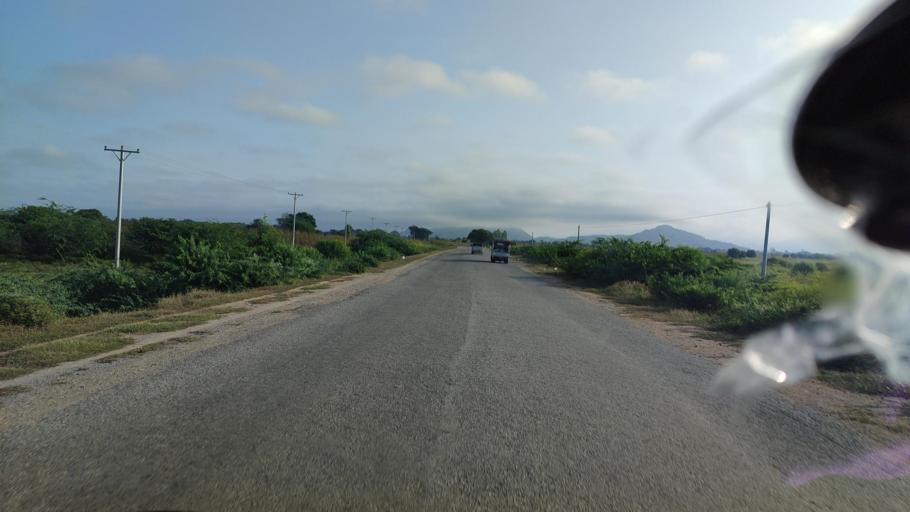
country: MM
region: Mandalay
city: Yamethin
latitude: 20.6847
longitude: 96.1540
